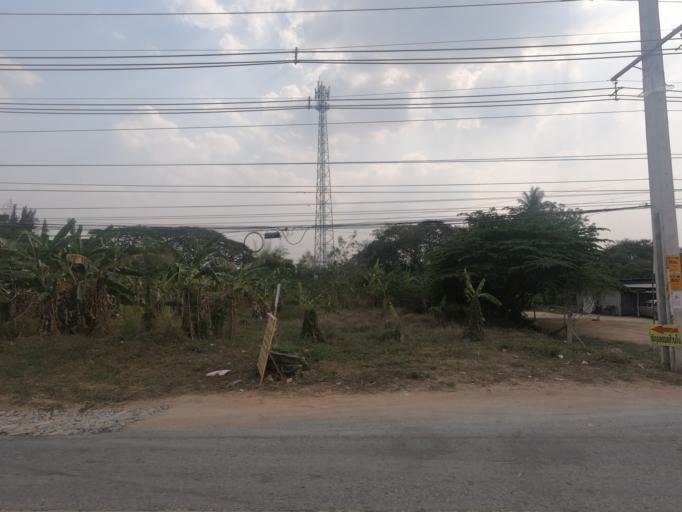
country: TH
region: Nakhon Ratchasima
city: Sikhio
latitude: 14.8697
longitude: 101.7608
